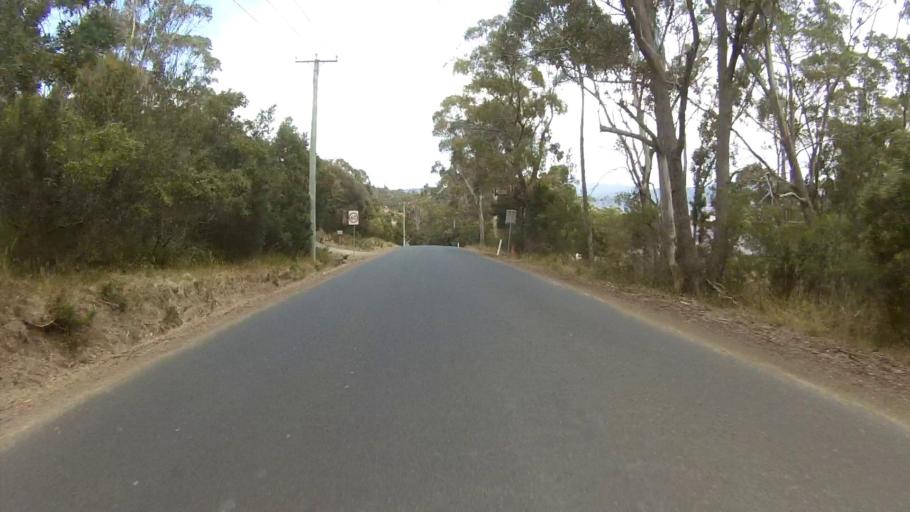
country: AU
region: Tasmania
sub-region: Kingborough
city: Blackmans Bay
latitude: -43.0287
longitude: 147.3123
